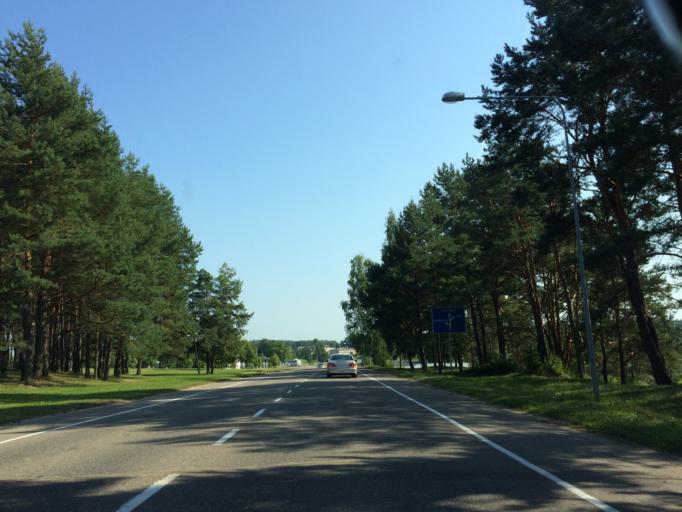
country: LV
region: Aglona
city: Aglona
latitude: 56.1284
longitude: 27.0094
